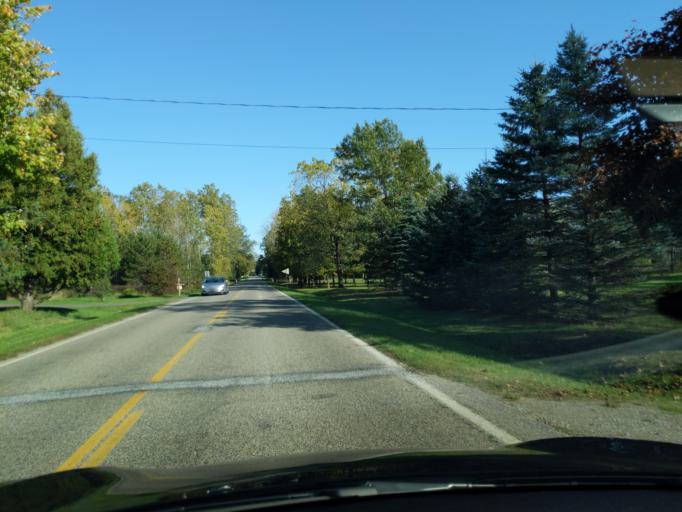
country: US
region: Michigan
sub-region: Shiawassee County
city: Laingsburg
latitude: 42.9290
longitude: -84.4490
